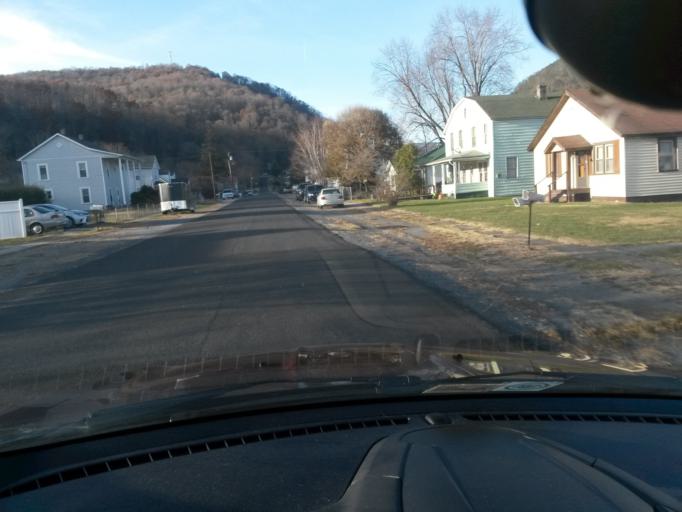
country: US
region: Virginia
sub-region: Alleghany County
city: Clifton Forge
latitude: 37.7994
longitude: -79.7913
